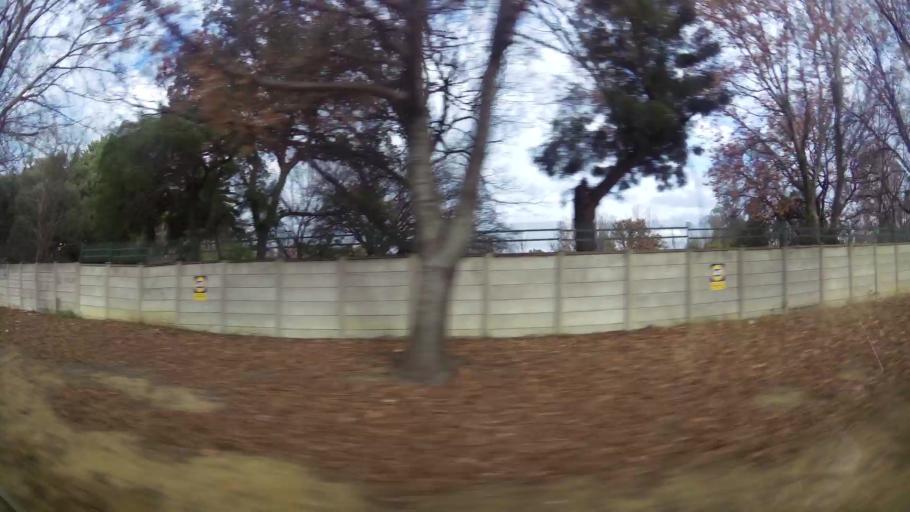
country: ZA
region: Orange Free State
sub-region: Fezile Dabi District Municipality
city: Sasolburg
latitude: -26.7973
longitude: 27.8225
